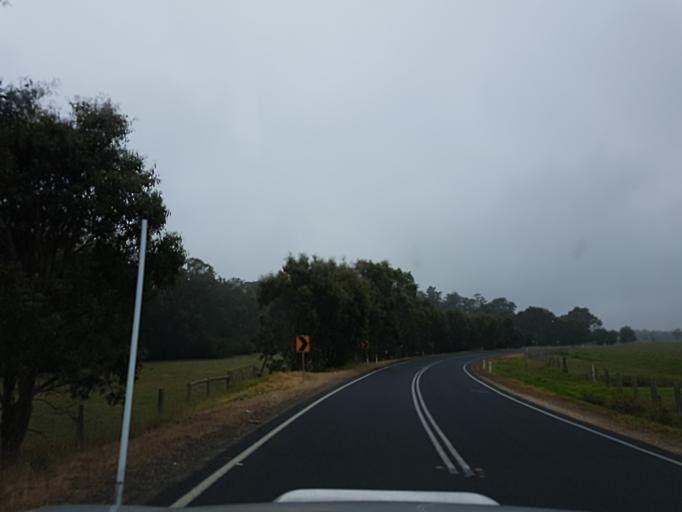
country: AU
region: Victoria
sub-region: Wellington
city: Sale
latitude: -38.0823
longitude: 147.0137
